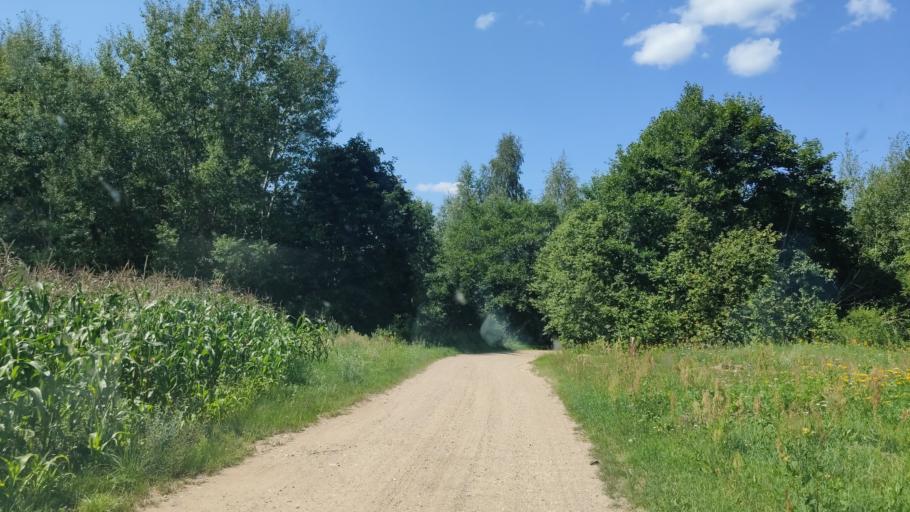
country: BY
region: Vitebsk
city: Byahoml'
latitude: 54.9709
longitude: 28.0243
